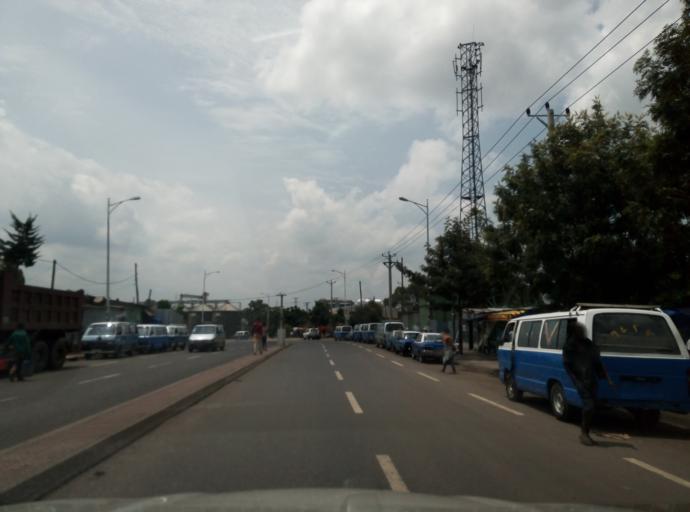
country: ET
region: Adis Abeba
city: Addis Ababa
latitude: 8.9452
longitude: 38.7571
